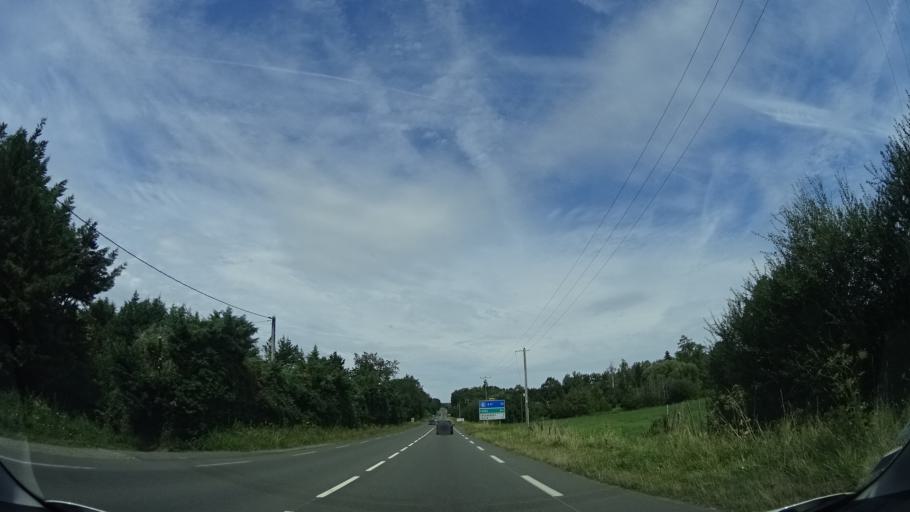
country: FR
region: Pays de la Loire
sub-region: Departement de la Sarthe
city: La Fleche
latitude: 47.7211
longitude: -0.1076
